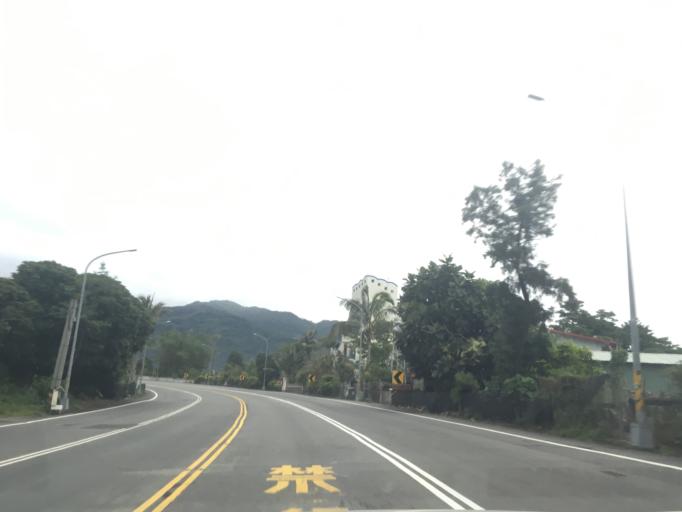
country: TW
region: Taiwan
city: Taitung City
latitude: 22.7463
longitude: 121.0570
